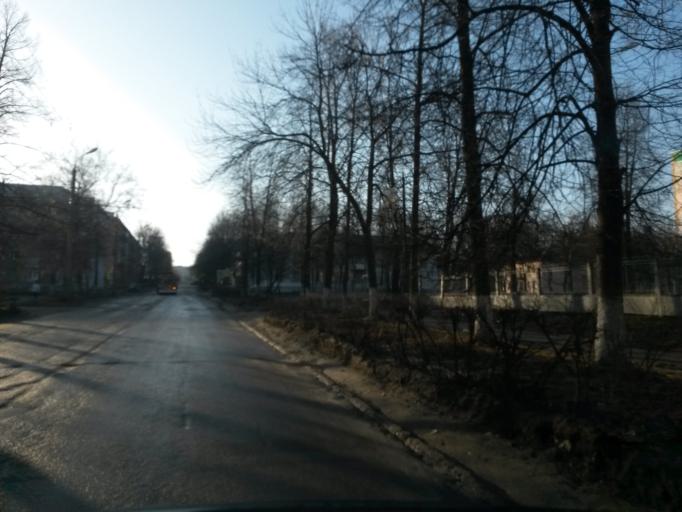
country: RU
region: Jaroslavl
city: Yaroslavl
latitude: 57.5829
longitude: 39.8404
